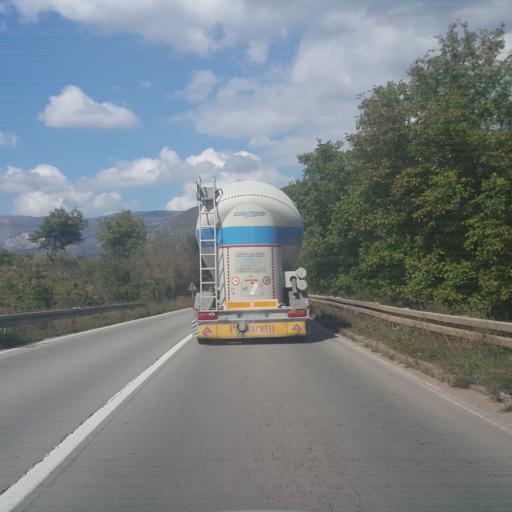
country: RS
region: Central Serbia
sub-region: Pirotski Okrug
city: Bela Palanka
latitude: 43.2857
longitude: 22.2196
